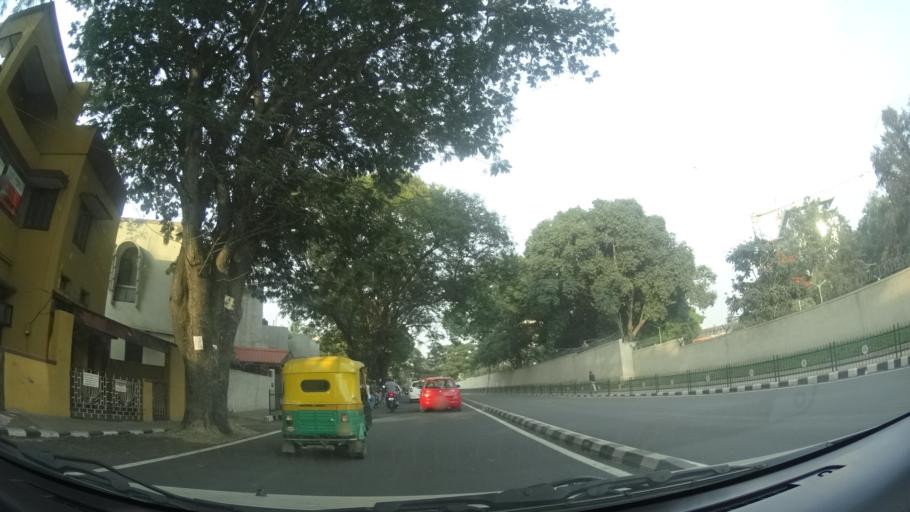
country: IN
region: Karnataka
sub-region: Bangalore Urban
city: Bangalore
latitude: 12.9980
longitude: 77.6260
